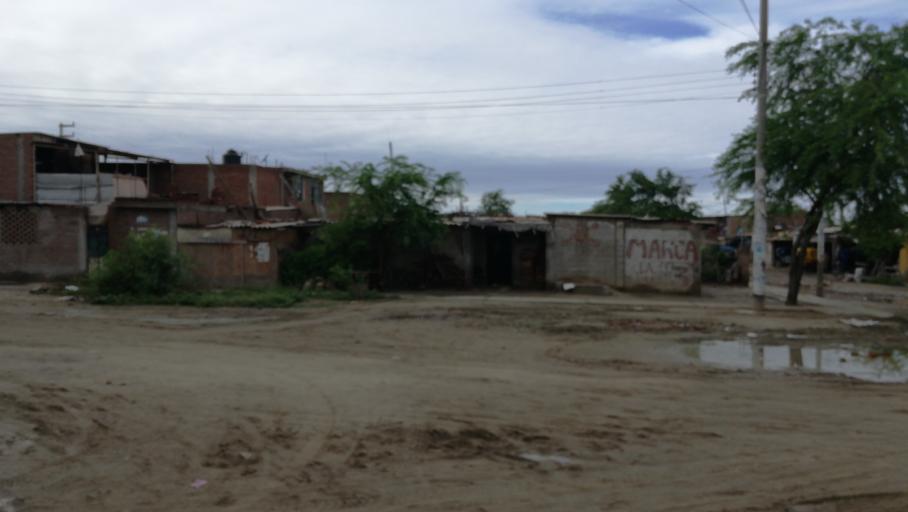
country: PE
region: Piura
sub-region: Provincia de Piura
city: Piura
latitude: -5.1867
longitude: -80.6730
